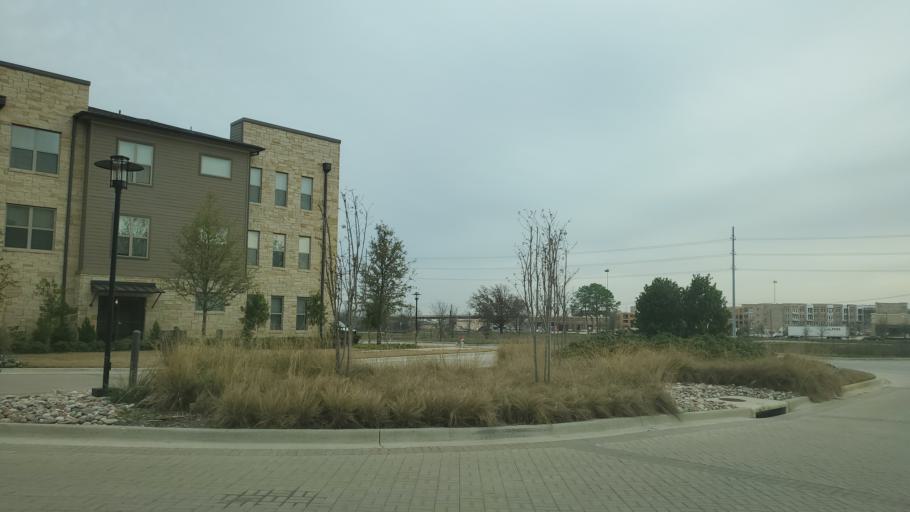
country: US
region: Texas
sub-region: Dallas County
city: Coppell
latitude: 32.9747
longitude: -97.0346
